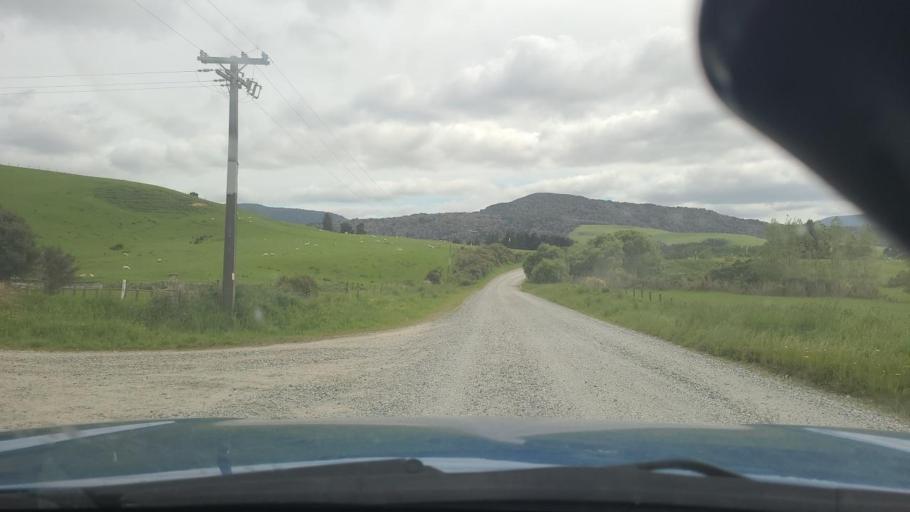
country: NZ
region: Otago
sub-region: Clutha District
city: Papatowai
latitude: -46.5311
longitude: 169.1298
